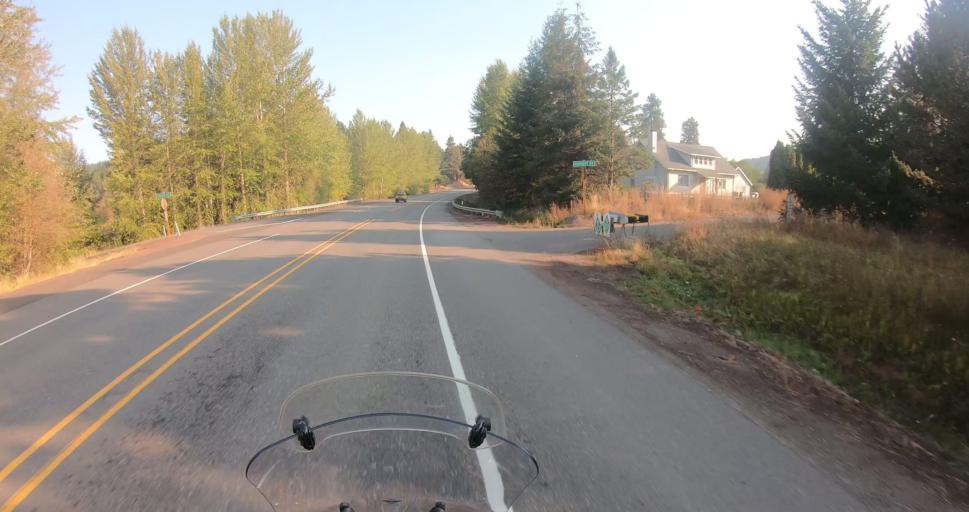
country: US
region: Oregon
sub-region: Hood River County
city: Odell
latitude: 45.5561
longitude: -121.5679
